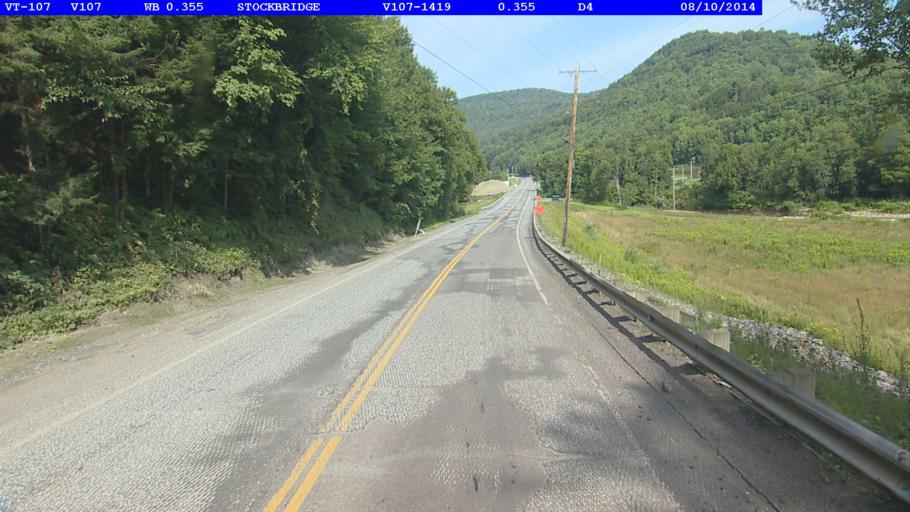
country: US
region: Vermont
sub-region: Orange County
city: Randolph
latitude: 43.7707
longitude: -72.7586
